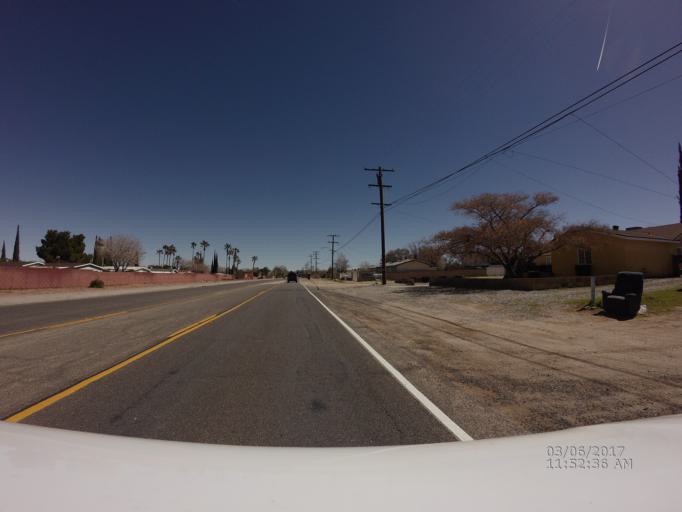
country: US
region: California
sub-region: Los Angeles County
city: Quartz Hill
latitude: 34.6456
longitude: -118.2340
